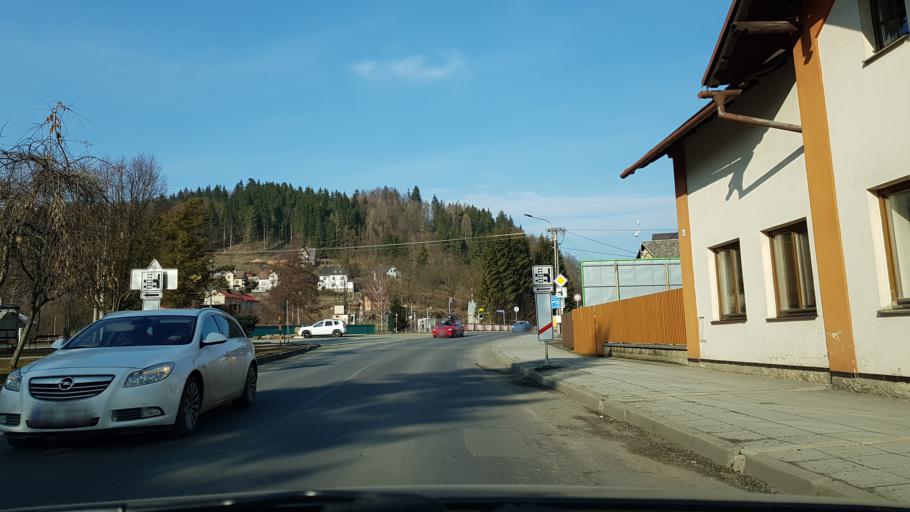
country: CZ
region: Olomoucky
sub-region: Okres Sumperk
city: Hanusovice
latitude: 50.0770
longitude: 16.9327
